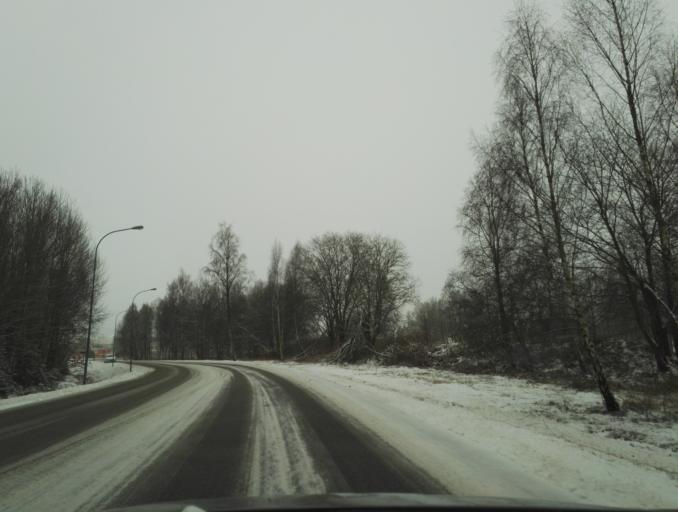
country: SE
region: Kronoberg
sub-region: Vaxjo Kommun
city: Vaexjoe
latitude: 56.8805
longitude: 14.7463
